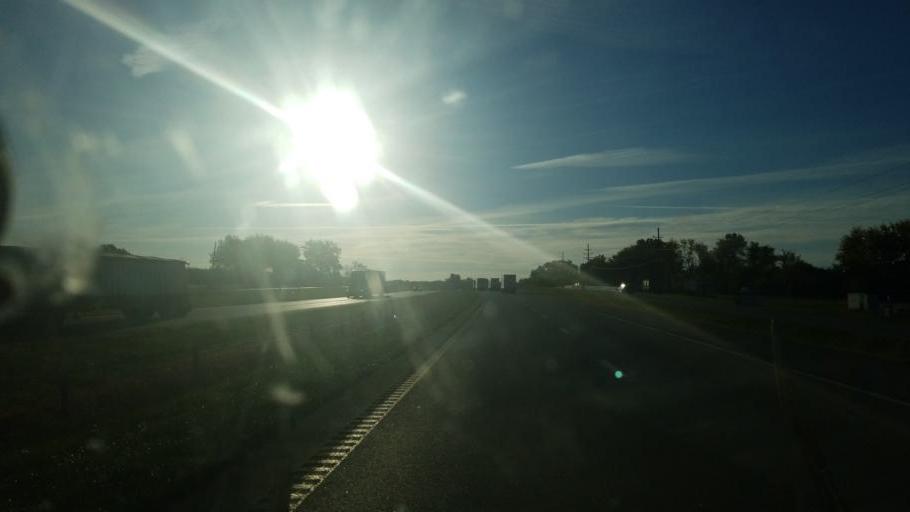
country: US
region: Missouri
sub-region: Warren County
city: Warrenton
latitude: 38.8314
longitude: -91.2160
